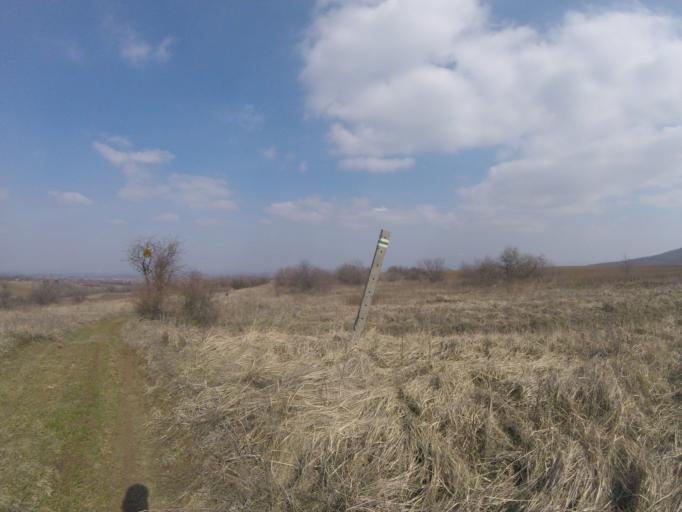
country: HU
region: Komarom-Esztergom
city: Nyergesujfalu
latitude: 47.7353
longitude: 18.5514
